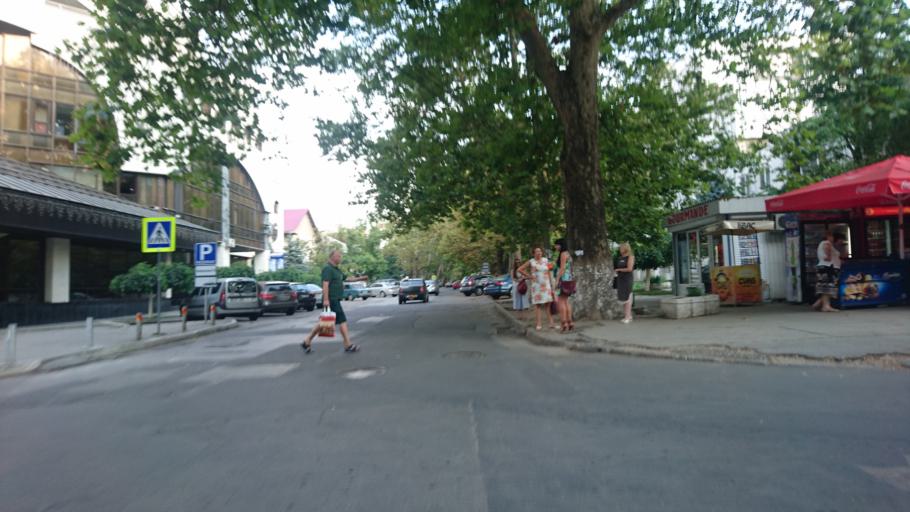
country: MD
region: Chisinau
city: Chisinau
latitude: 47.0180
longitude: 28.8364
